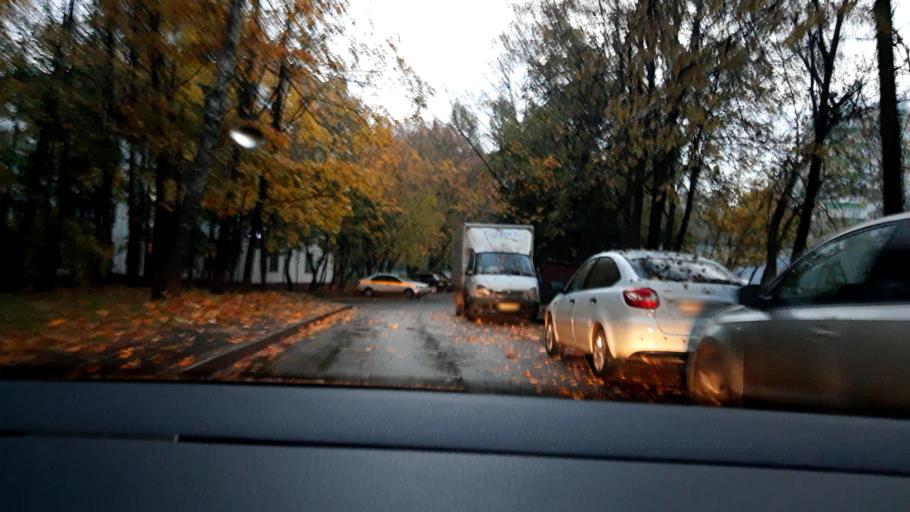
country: RU
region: Moscow
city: Gol'yanovo
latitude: 55.8182
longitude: 37.8178
